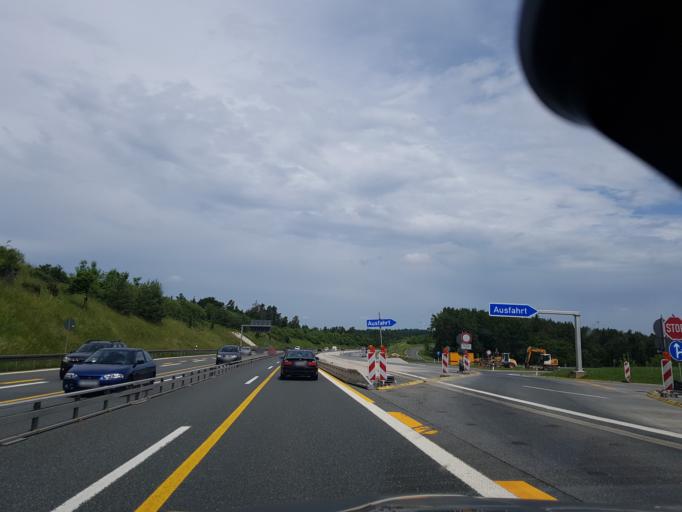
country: DE
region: Bavaria
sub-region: Upper Franconia
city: Haag
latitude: 49.8277
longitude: 11.4995
